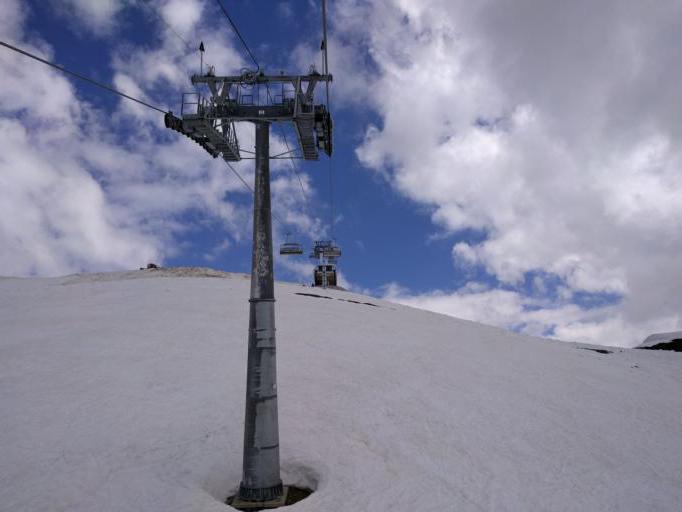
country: RU
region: Krasnodarskiy
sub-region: Sochi City
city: Krasnaya Polyana
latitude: 43.6221
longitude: 40.3104
